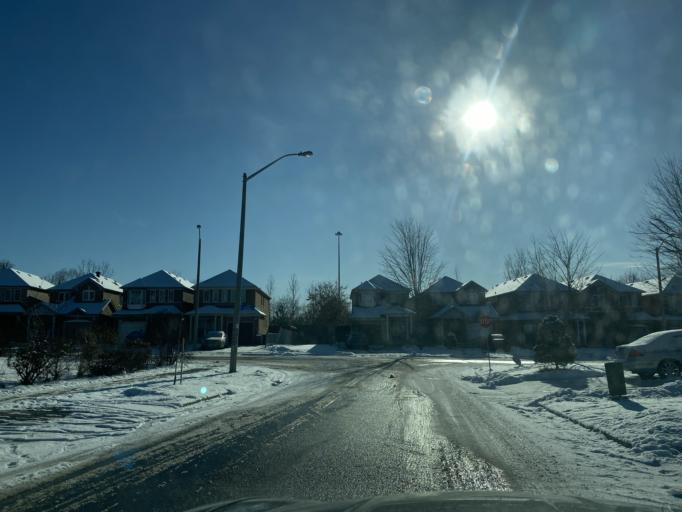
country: CA
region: Ontario
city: Scarborough
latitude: 43.7708
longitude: -79.3096
